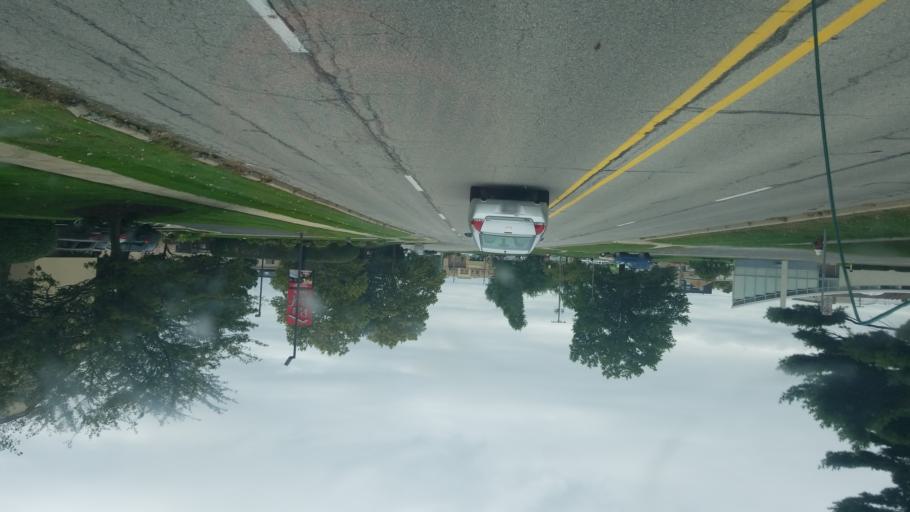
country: US
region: Ohio
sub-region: Lucas County
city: Ottawa Hills
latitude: 41.6826
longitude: -83.6260
